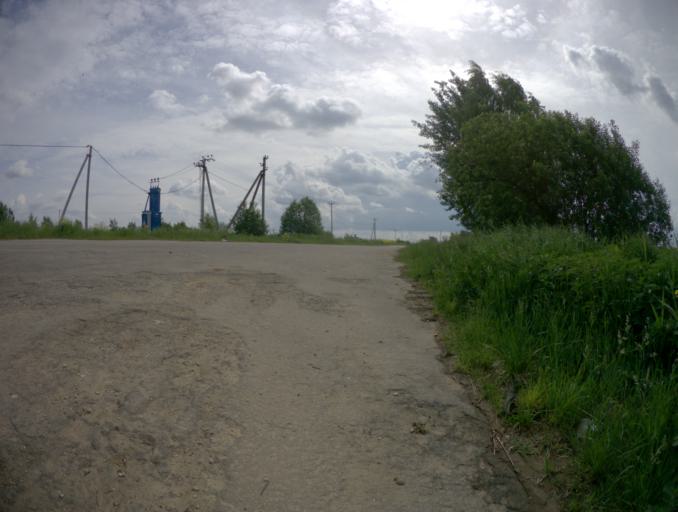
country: RU
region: Vladimir
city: Stavrovo
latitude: 56.0983
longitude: 39.9662
